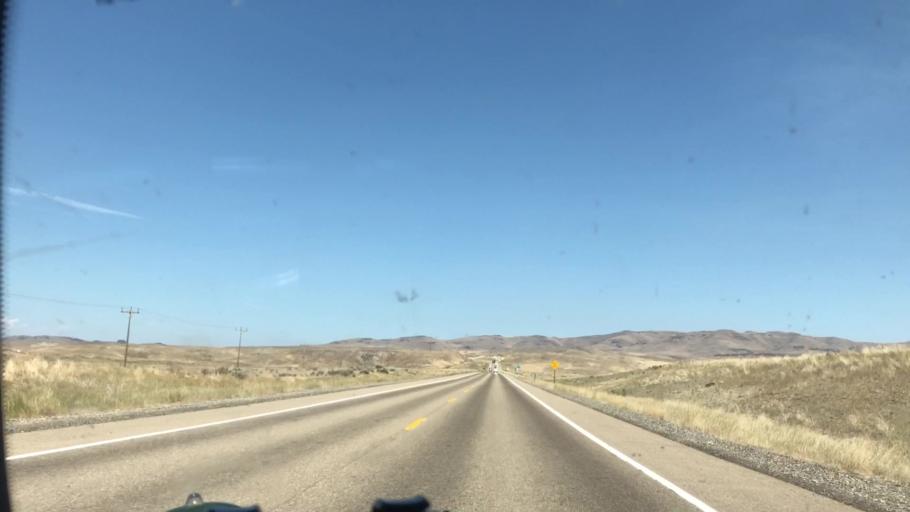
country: US
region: Idaho
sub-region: Owyhee County
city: Marsing
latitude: 43.2546
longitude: -117.0196
